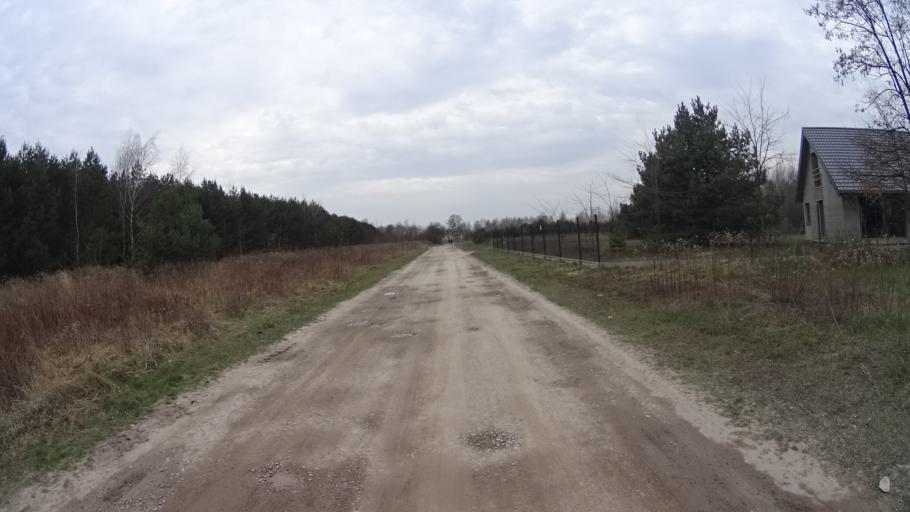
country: PL
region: Masovian Voivodeship
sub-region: Powiat warszawski zachodni
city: Jozefow
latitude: 52.2459
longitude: 20.6850
